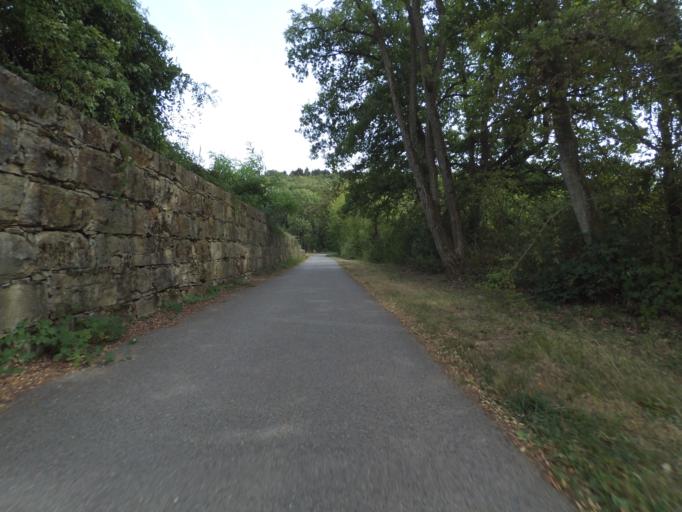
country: LU
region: Grevenmacher
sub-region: Canton de Remich
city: Bous
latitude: 49.5350
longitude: 6.3348
